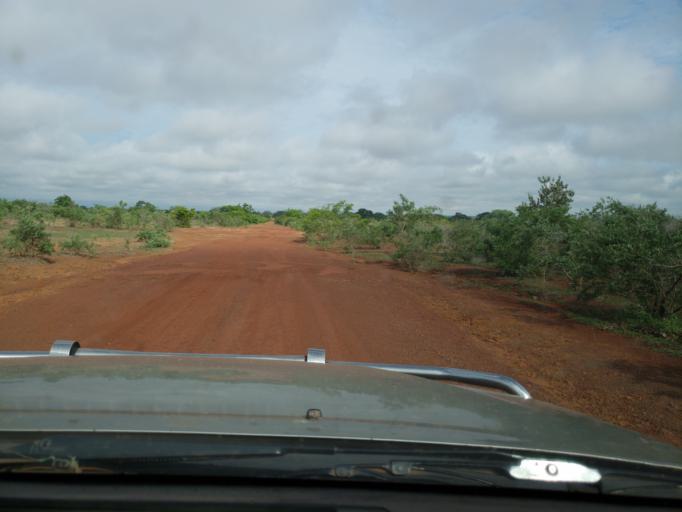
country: ML
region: Sikasso
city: Koutiala
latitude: 12.3924
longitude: -5.9950
